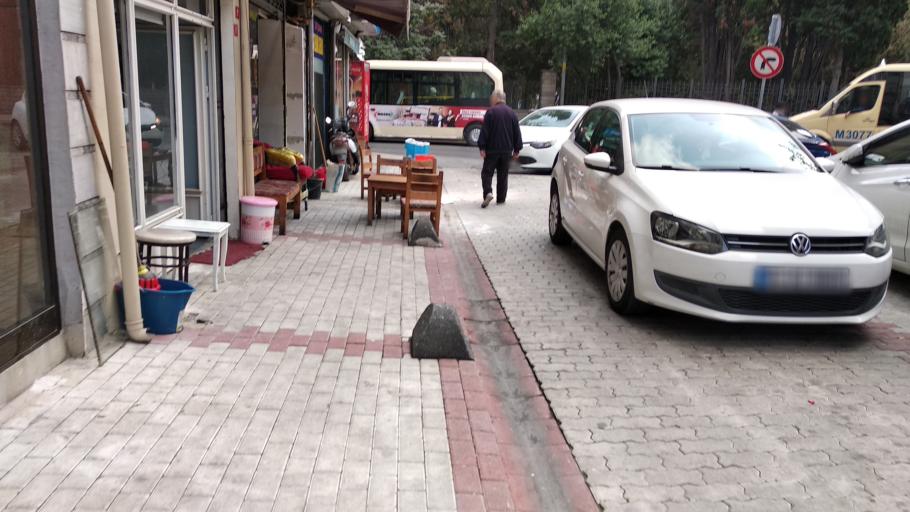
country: TR
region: Istanbul
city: Bahcelievler
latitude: 40.9824
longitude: 28.8723
